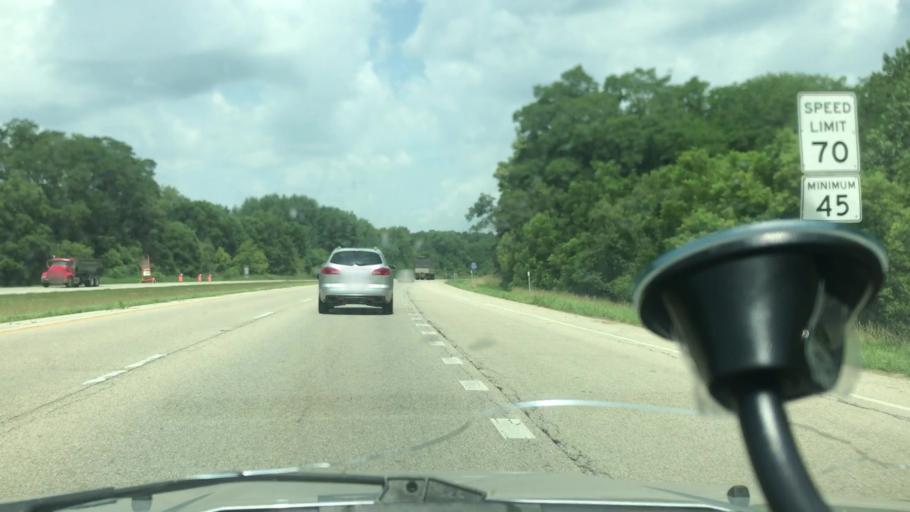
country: US
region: Illinois
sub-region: Peoria County
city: Bellevue
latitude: 40.6737
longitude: -89.6704
